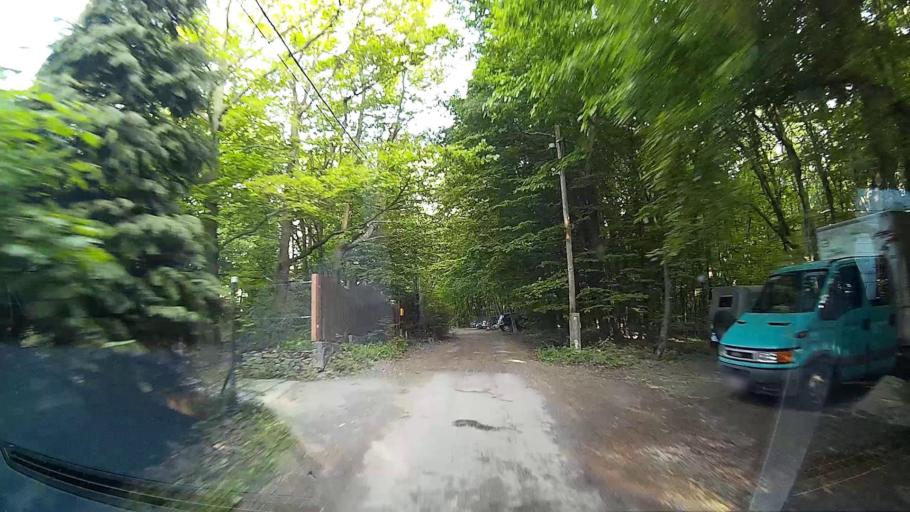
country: HU
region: Pest
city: Visegrad
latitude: 47.7180
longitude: 18.9898
